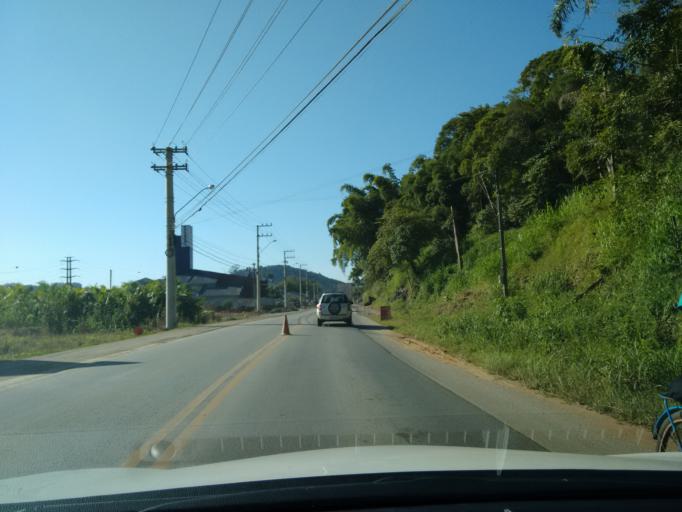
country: BR
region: Santa Catarina
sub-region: Jaragua Do Sul
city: Jaragua do Sul
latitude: -26.5233
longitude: -49.1304
